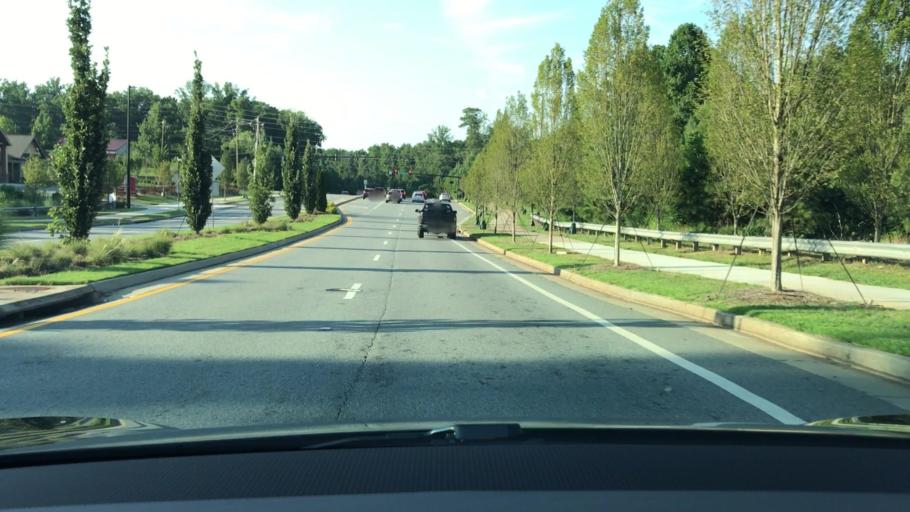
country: US
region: Georgia
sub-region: Fulton County
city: Alpharetta
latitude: 34.0731
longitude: -84.2719
